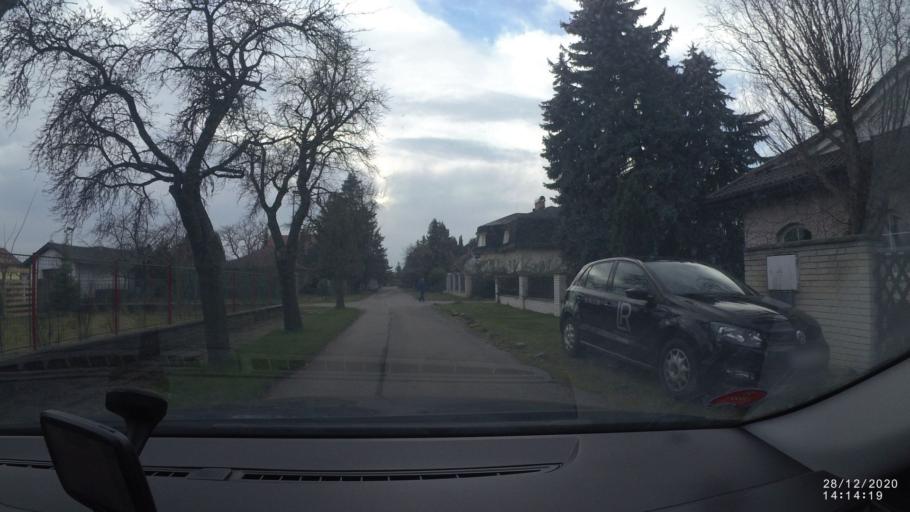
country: CZ
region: Central Bohemia
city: Sestajovice
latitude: 50.1028
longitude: 14.6606
